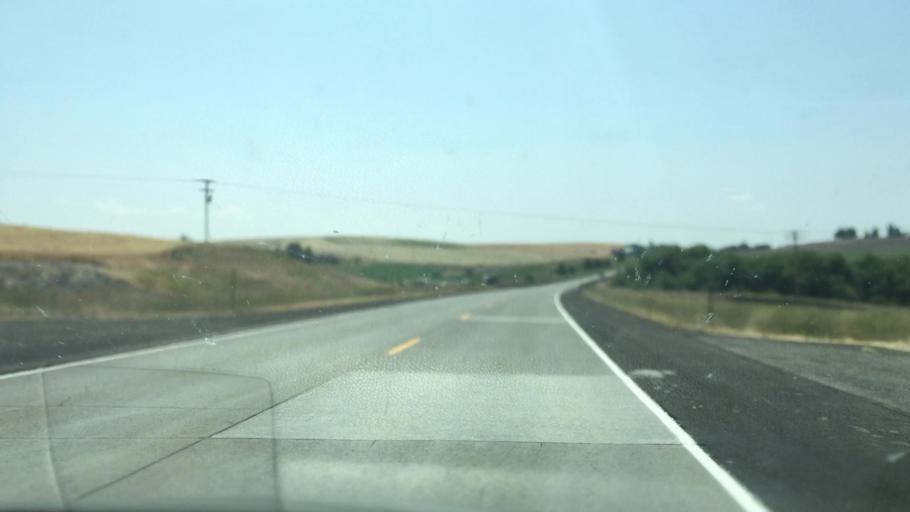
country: US
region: Idaho
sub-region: Lewis County
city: Nezperce
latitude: 46.0713
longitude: -116.3416
